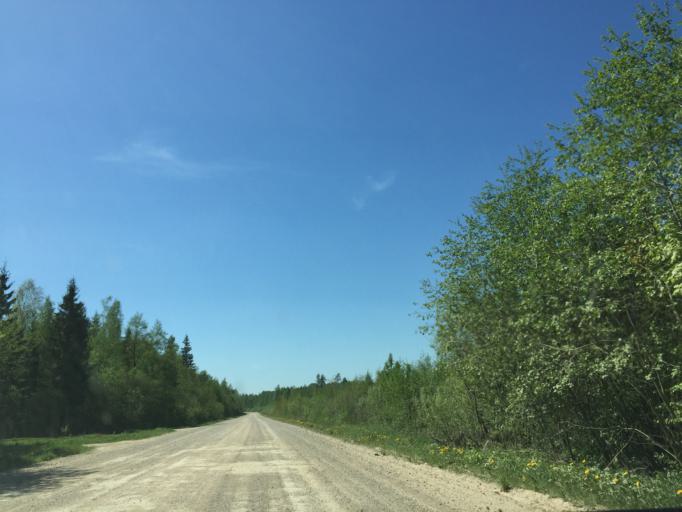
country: LV
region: Kegums
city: Kegums
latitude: 56.8820
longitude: 24.7850
